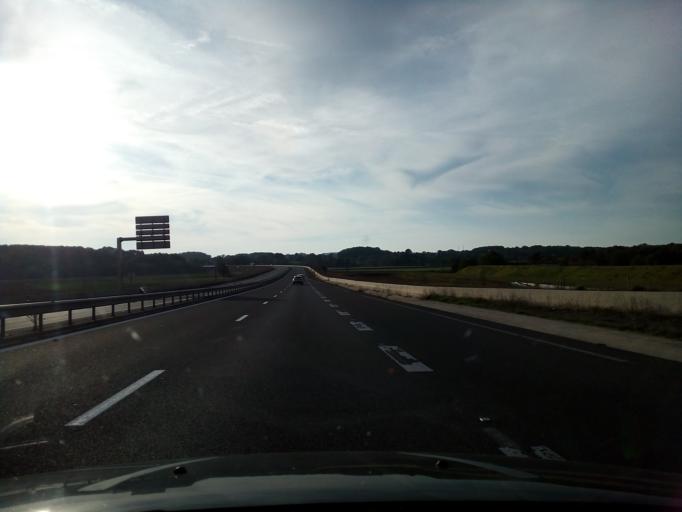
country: FR
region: Poitou-Charentes
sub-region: Departement de la Charente
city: La Rochefoucauld
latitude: 45.7534
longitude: 0.3802
